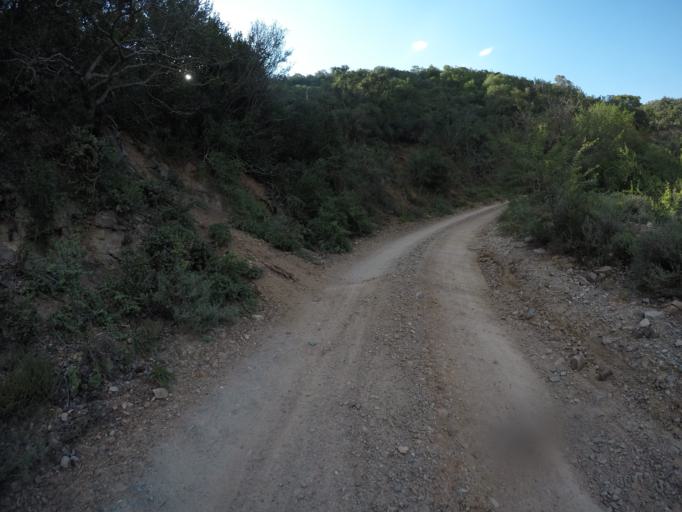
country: ZA
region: Eastern Cape
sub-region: Cacadu District Municipality
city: Kareedouw
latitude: -33.6504
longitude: 24.3487
